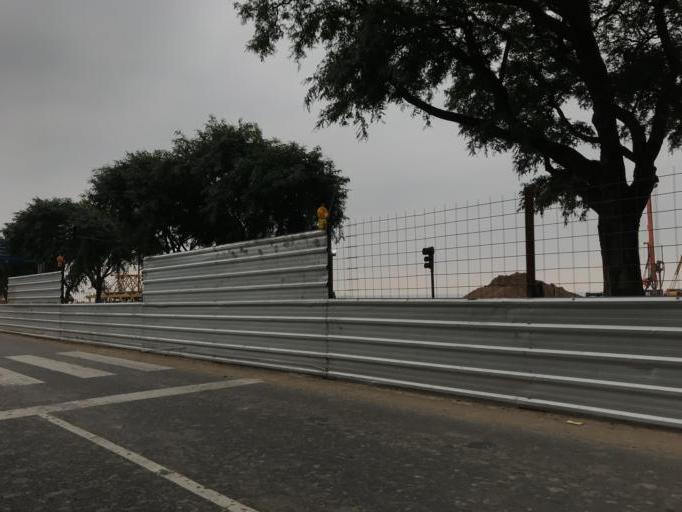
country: AR
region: Buenos Aires F.D.
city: Retiro
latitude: -34.5572
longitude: -58.4122
